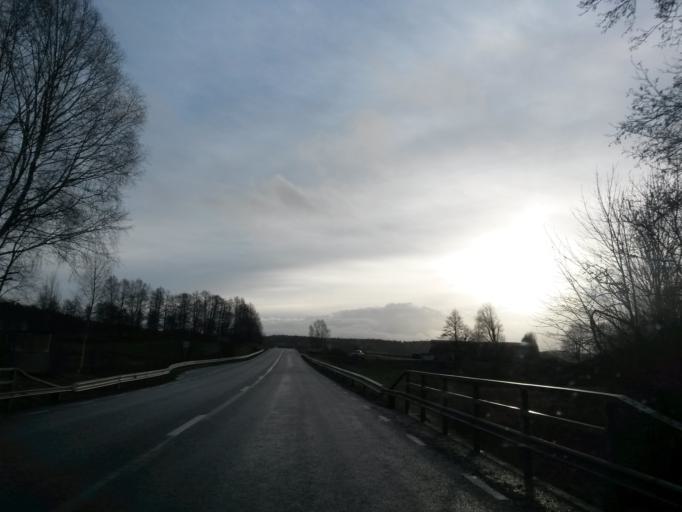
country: SE
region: Vaestra Goetaland
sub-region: Harryda Kommun
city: Ravlanda
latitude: 57.5268
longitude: 12.5390
